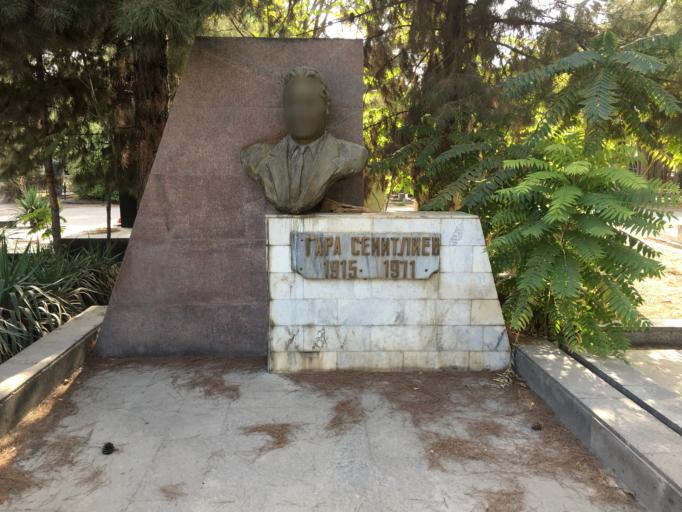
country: TM
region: Ahal
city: Ashgabat
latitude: 37.9704
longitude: 58.3558
